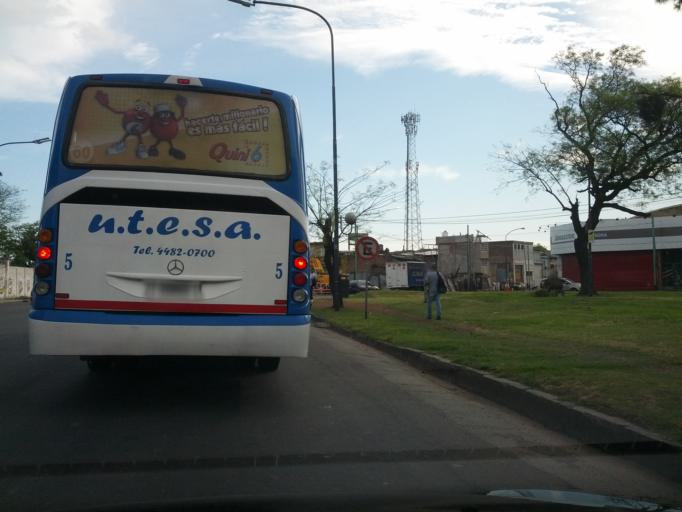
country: AR
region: Buenos Aires
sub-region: Partido de Avellaneda
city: Avellaneda
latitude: -34.6472
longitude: -58.4029
